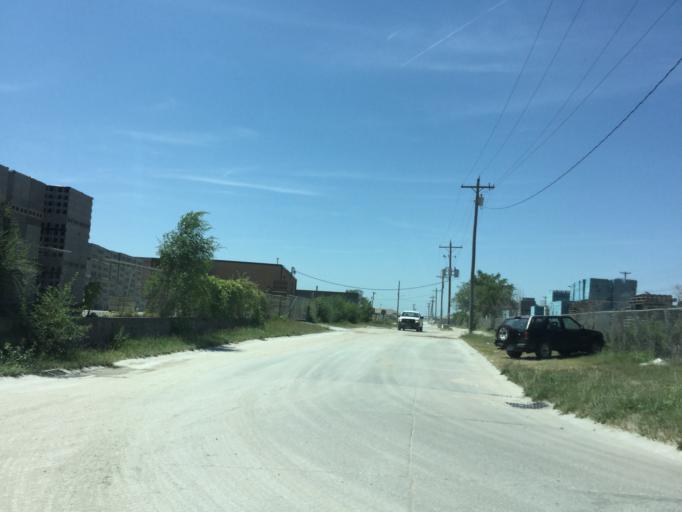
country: US
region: Kansas
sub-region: Shawnee County
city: Topeka
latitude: 39.0680
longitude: -95.6744
